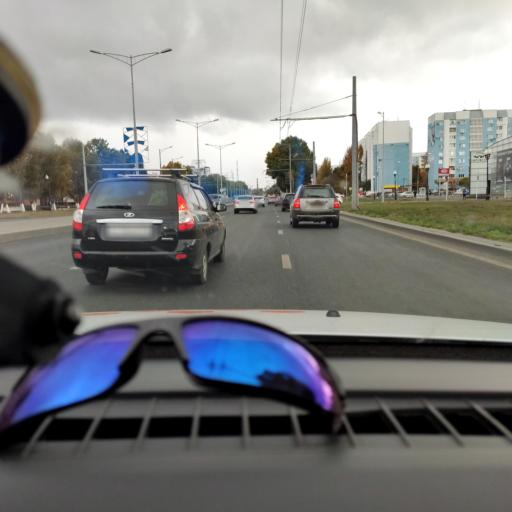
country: RU
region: Samara
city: Samara
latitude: 53.2486
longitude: 50.2183
